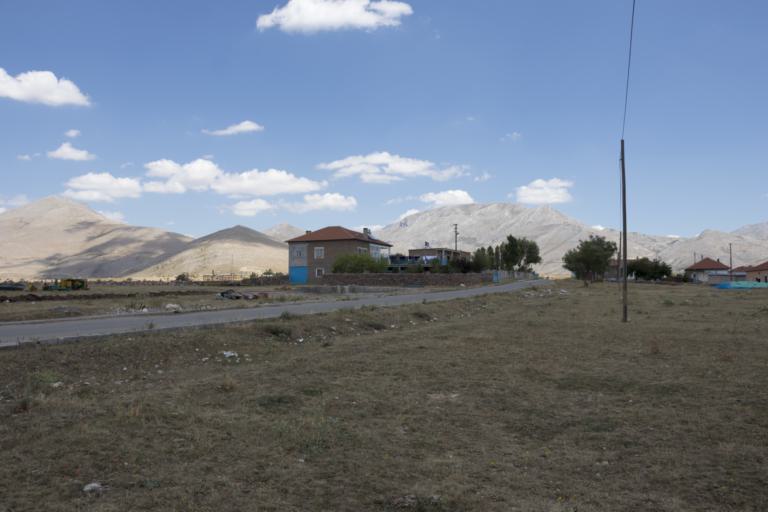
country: TR
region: Kayseri
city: Toklar
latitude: 38.4089
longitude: 36.0810
